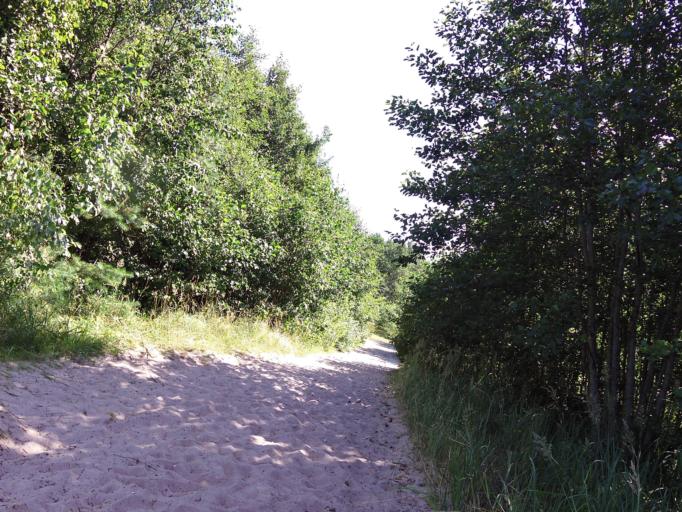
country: EE
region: Hiiumaa
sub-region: Kaerdla linn
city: Kardla
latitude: 58.9345
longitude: 22.3889
